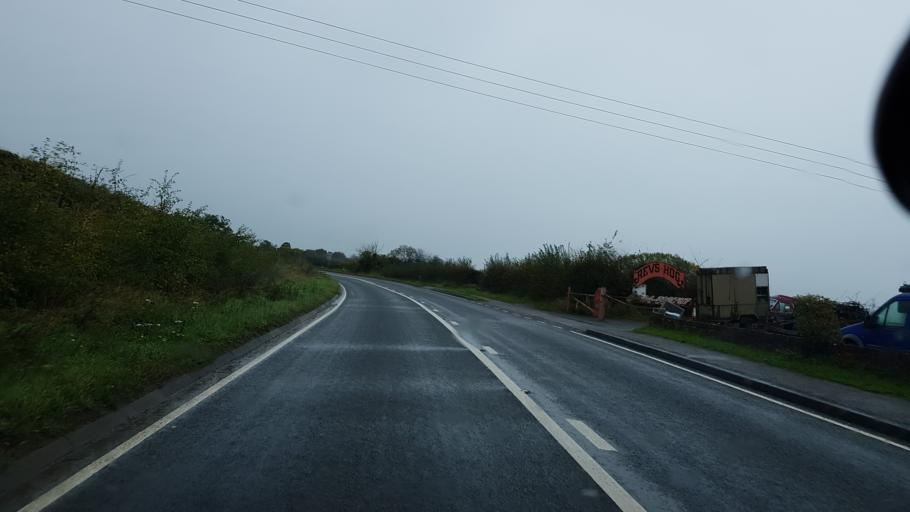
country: GB
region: England
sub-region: Worcestershire
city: Upton upon Severn
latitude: 52.0679
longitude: -2.1952
